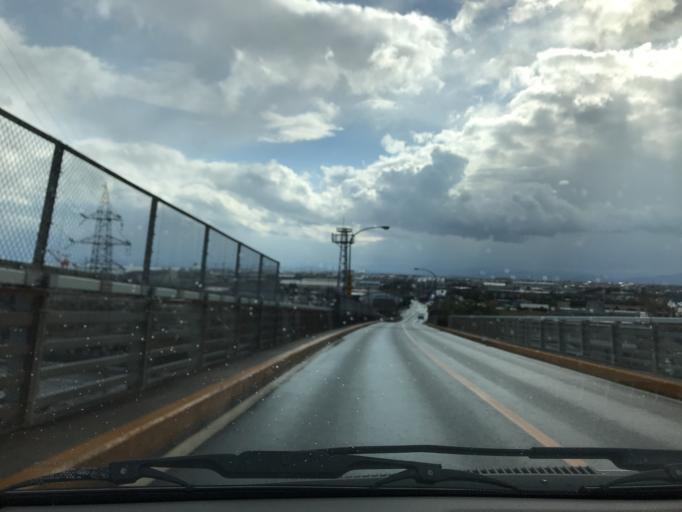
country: JP
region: Shimane
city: Sakaiminato
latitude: 35.5459
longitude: 133.2458
